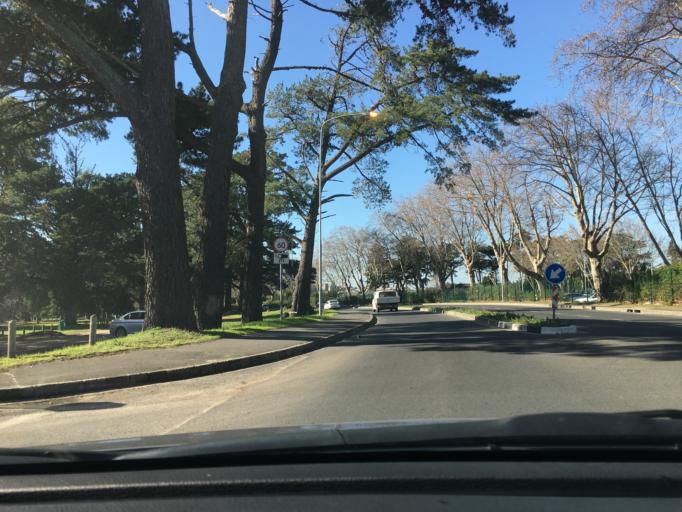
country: ZA
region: Western Cape
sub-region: City of Cape Town
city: Bergvliet
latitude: -34.0194
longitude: 18.4473
